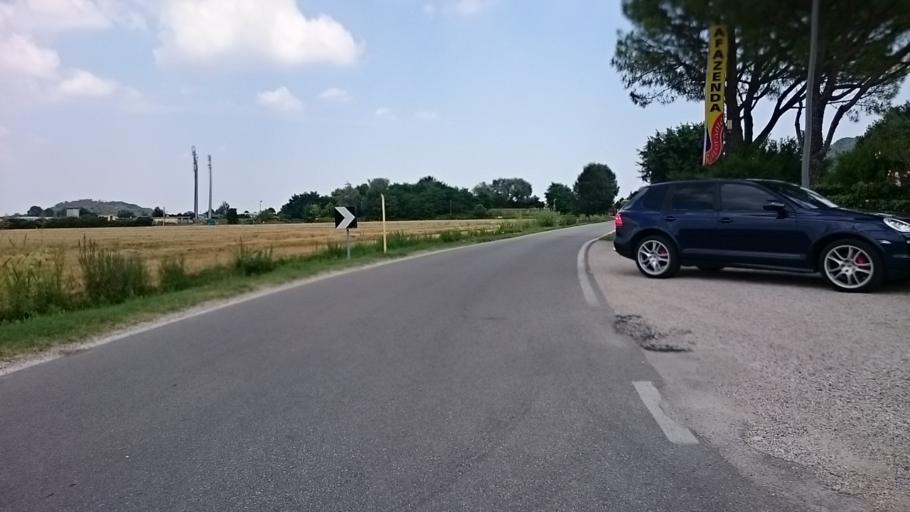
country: IT
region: Veneto
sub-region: Provincia di Padova
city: Torreglia
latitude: 45.3322
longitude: 11.7410
